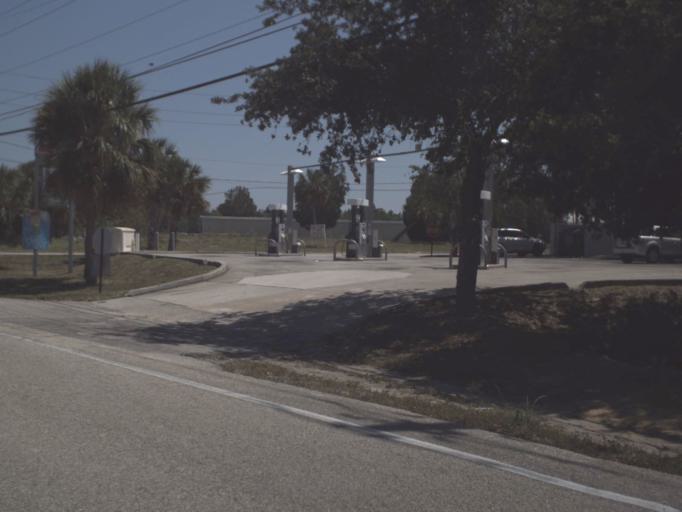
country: US
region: Florida
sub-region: Brevard County
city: Micco
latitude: 27.8809
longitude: -80.5017
